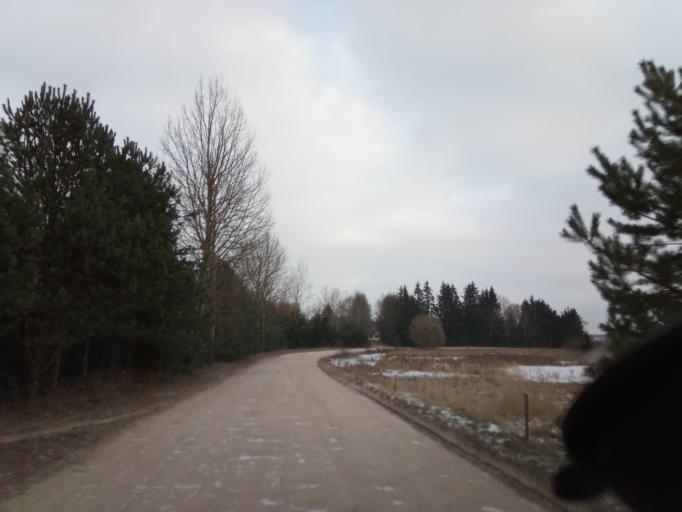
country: LT
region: Alytaus apskritis
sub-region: Alytaus rajonas
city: Daugai
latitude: 54.3628
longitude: 24.4424
